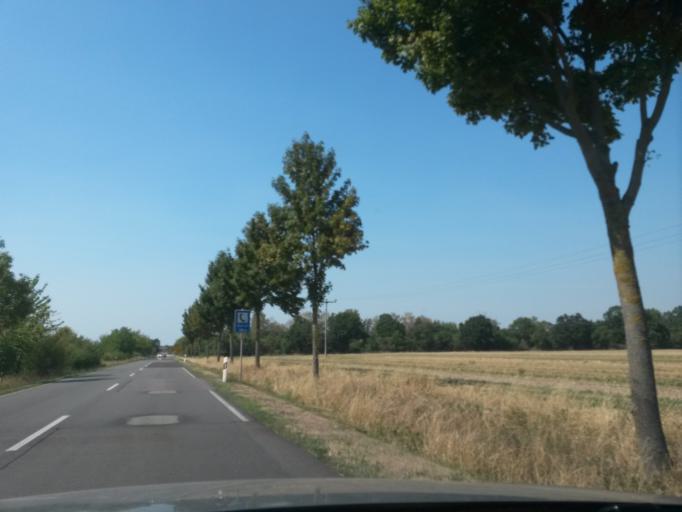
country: DE
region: Saxony-Anhalt
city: Tucheim
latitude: 52.3097
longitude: 12.1412
